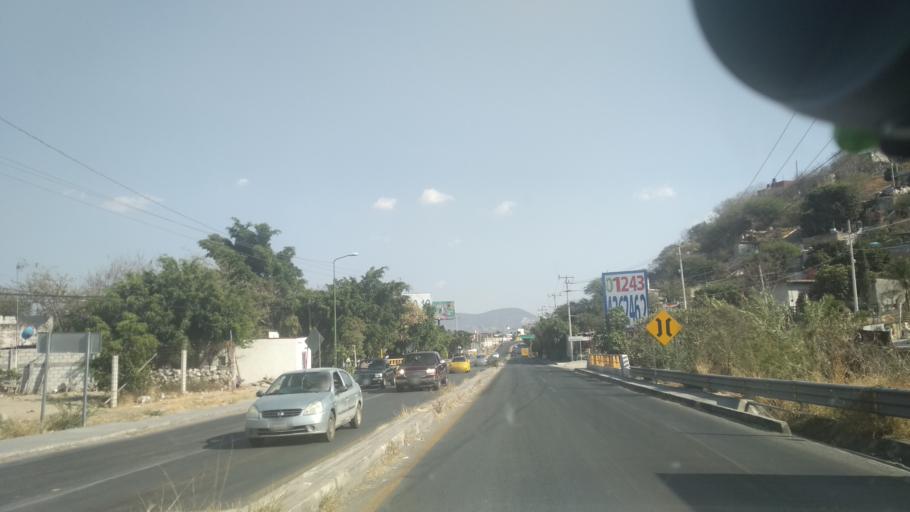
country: MX
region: Puebla
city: Izucar de Matamoros
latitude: 18.6154
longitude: -98.4678
